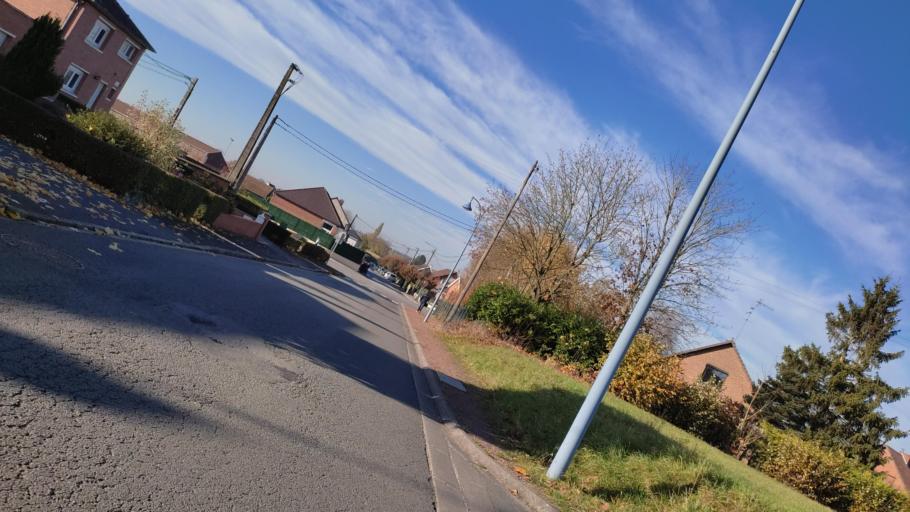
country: FR
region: Nord-Pas-de-Calais
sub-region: Departement du Pas-de-Calais
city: Agny
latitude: 50.2557
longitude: 2.7590
